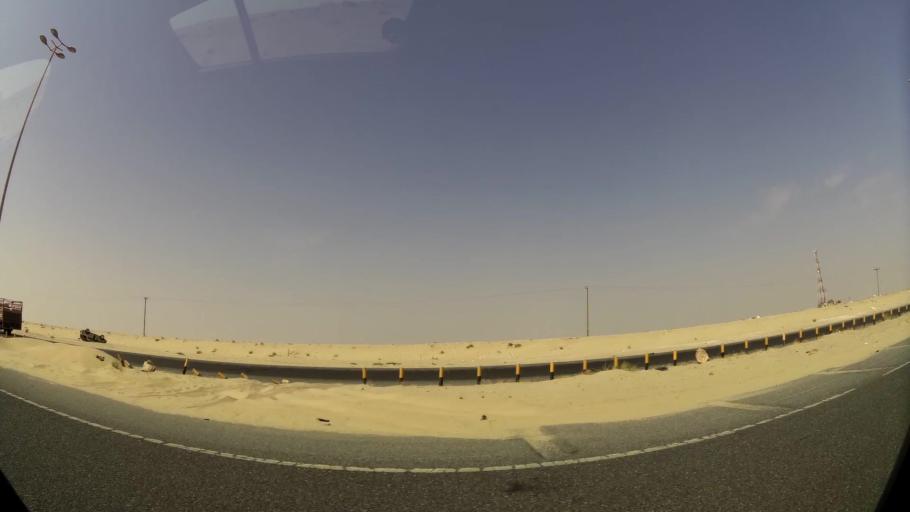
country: KW
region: Al Ahmadi
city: Al Wafrah
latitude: 28.8387
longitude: 48.0580
